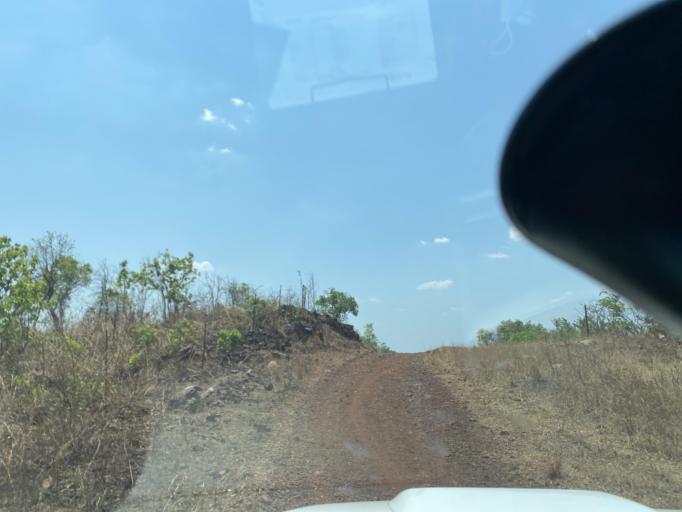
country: ZM
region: Lusaka
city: Lusaka
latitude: -15.4996
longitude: 27.9692
